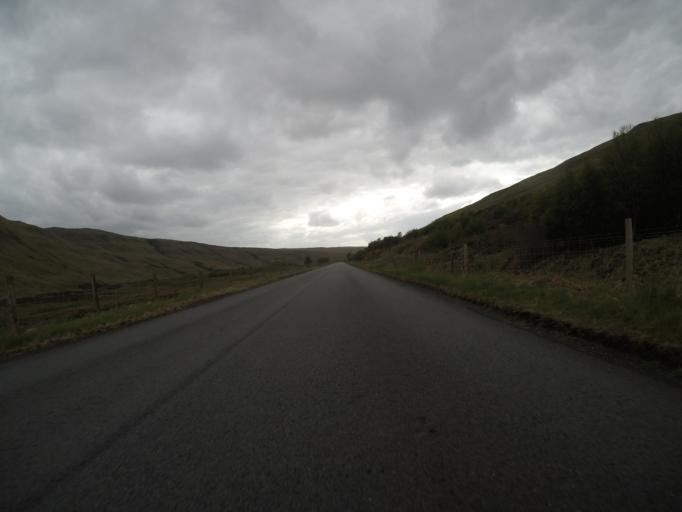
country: GB
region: Scotland
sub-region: Highland
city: Isle of Skye
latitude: 57.3004
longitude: -6.2545
